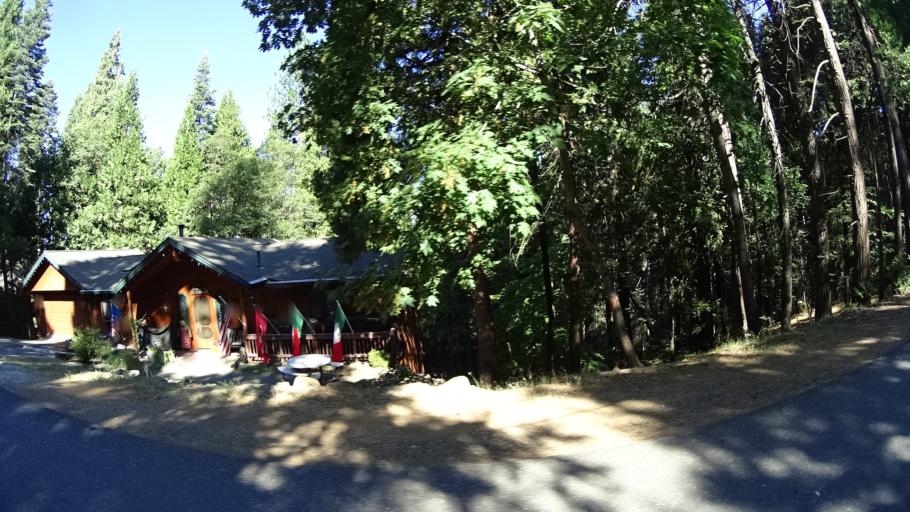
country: US
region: California
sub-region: Calaveras County
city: Arnold
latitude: 38.2609
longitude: -120.3200
